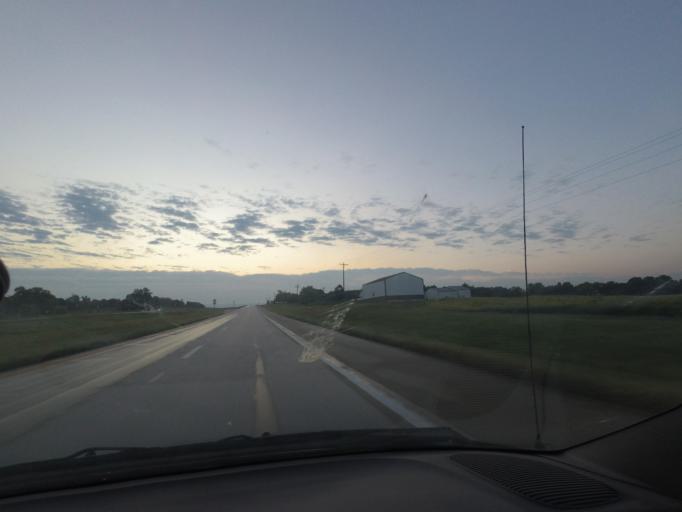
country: US
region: Missouri
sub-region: Macon County
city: Macon
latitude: 39.7595
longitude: -92.6708
